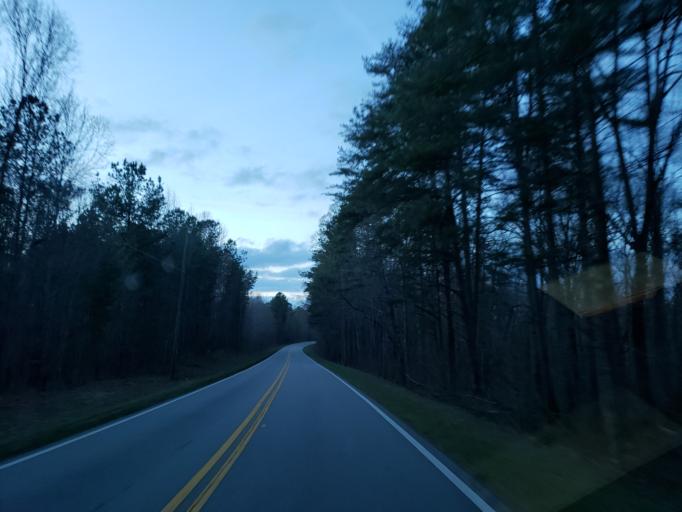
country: US
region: Georgia
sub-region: Paulding County
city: Dallas
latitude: 33.9955
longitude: -84.9240
